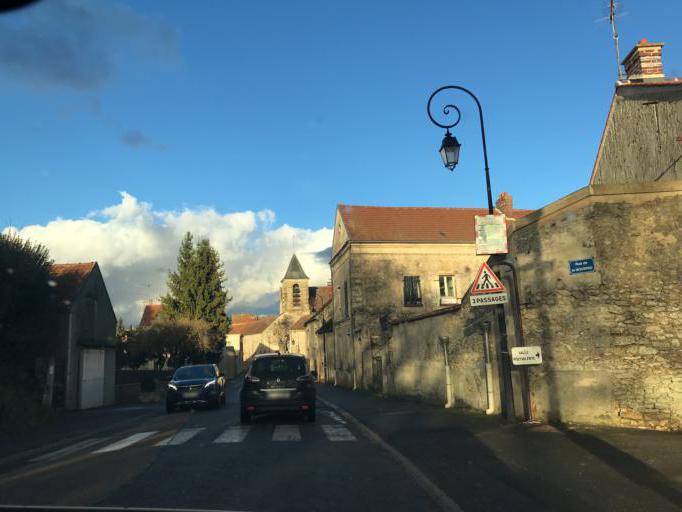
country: FR
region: Ile-de-France
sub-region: Departement de Seine-et-Marne
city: Juilly
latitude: 49.0002
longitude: 2.7030
